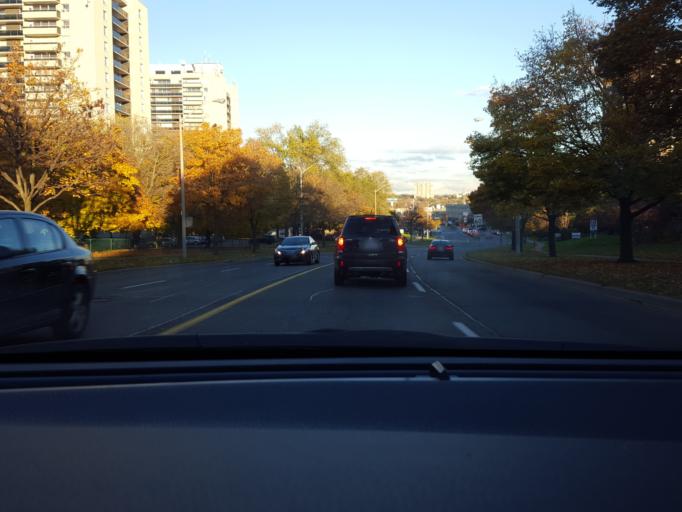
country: CA
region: Ontario
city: Willowdale
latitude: 43.7529
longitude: -79.3635
